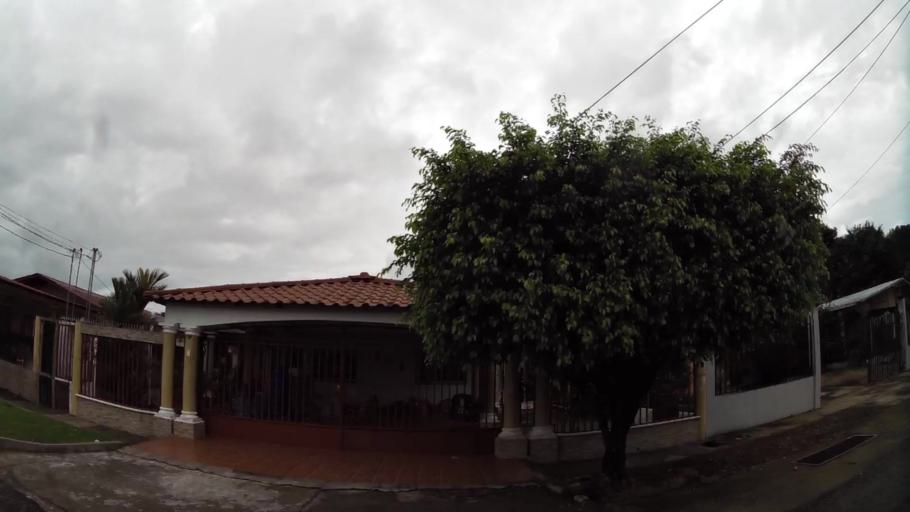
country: PA
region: Chiriqui
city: David
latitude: 8.4017
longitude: -82.4599
